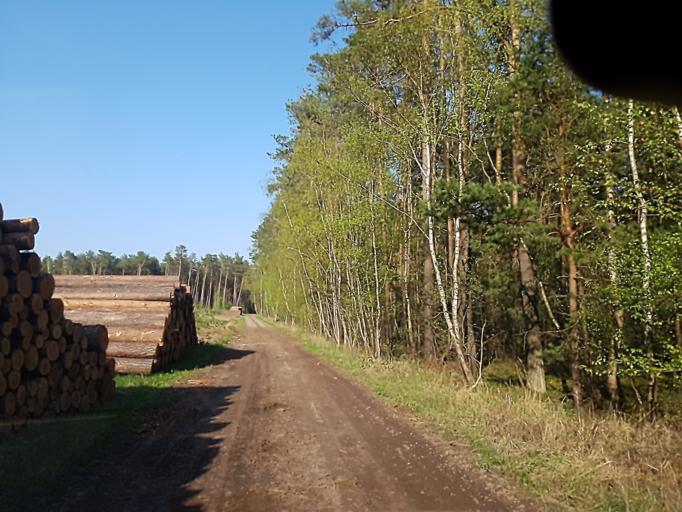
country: DE
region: Brandenburg
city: Bad Liebenwerda
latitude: 51.5574
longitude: 13.3780
